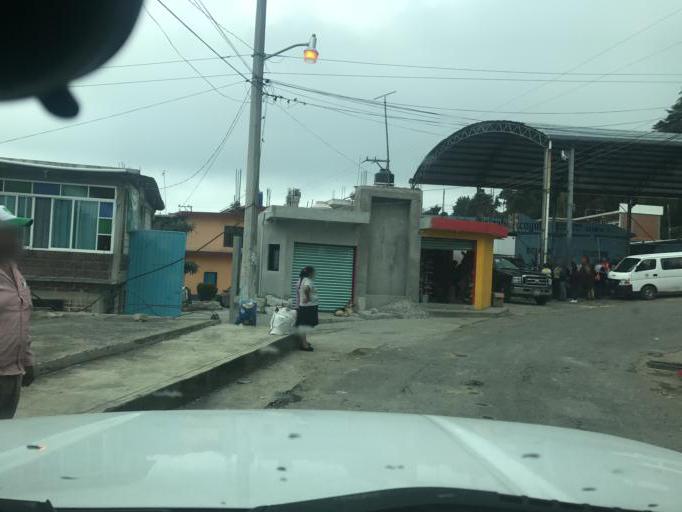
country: MX
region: Morelos
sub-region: Ocuituco
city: Huepalcalco (San Miguel)
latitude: 18.8986
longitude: -98.7553
